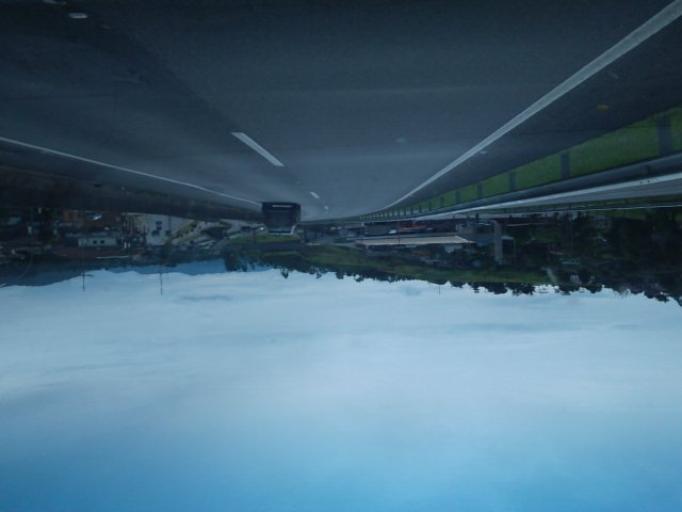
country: BR
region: Sao Paulo
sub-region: Cajati
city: Cajati
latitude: -24.7310
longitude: -48.0997
